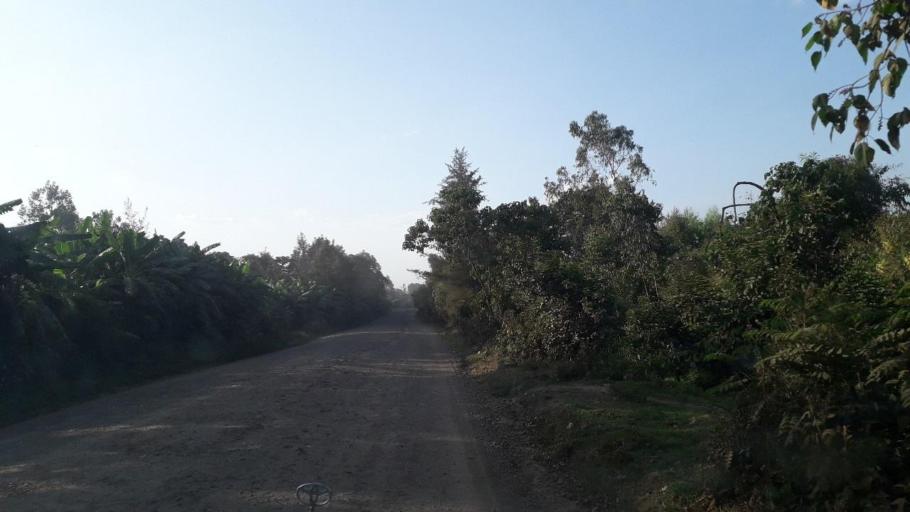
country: ET
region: Oromiya
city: Jima
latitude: 7.5892
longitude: 36.8566
